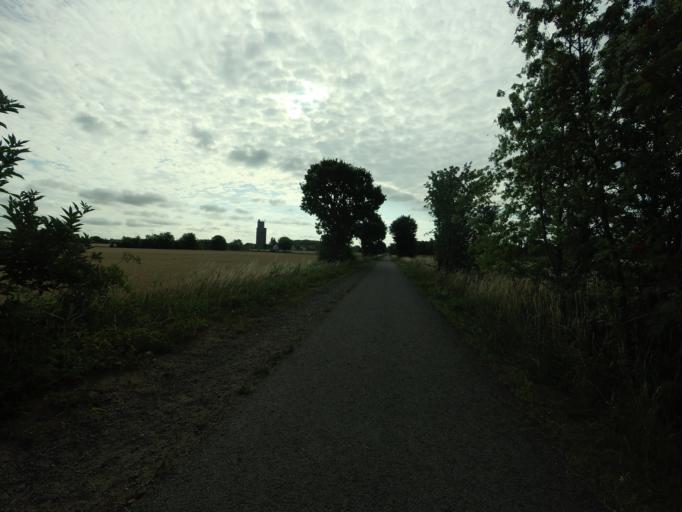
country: SE
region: Skane
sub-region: Helsingborg
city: Odakra
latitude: 56.1786
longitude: 12.6713
